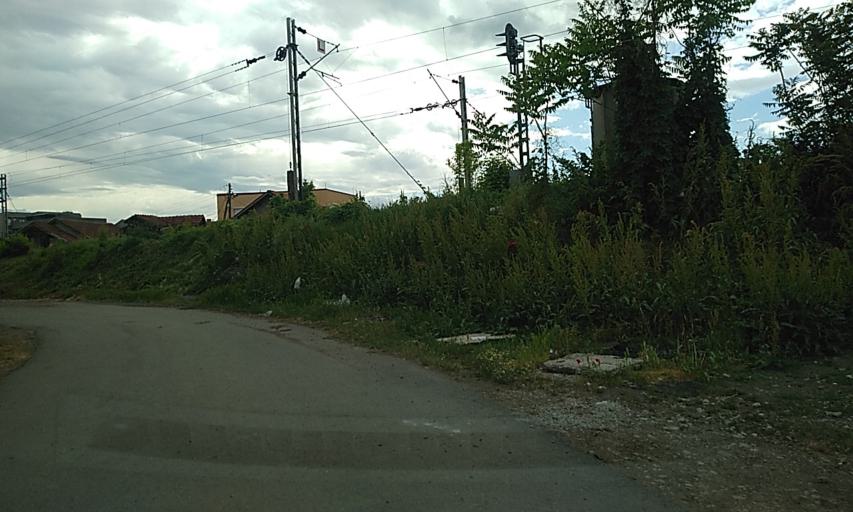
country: RS
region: Central Serbia
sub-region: Nisavski Okrug
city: Nis
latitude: 43.3211
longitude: 21.8873
